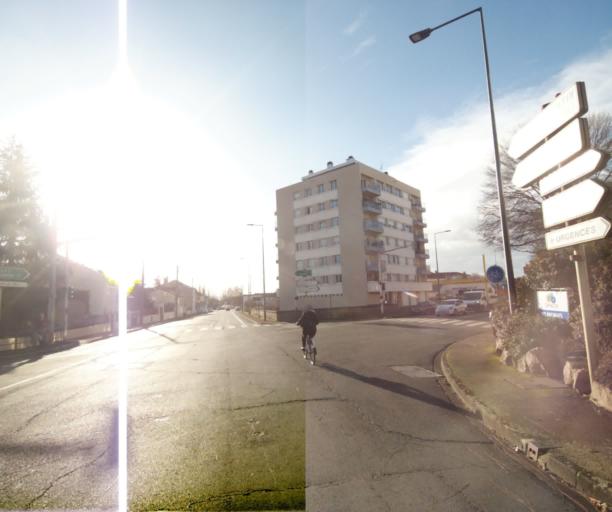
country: FR
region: Rhone-Alpes
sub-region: Departement de la Loire
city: Le Coteau
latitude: 46.0422
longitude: 4.0816
